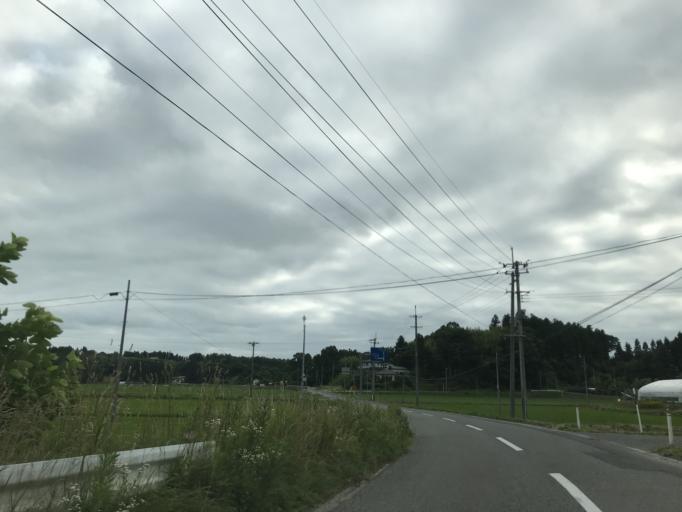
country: JP
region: Iwate
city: Ichinoseki
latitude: 38.7908
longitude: 141.2402
